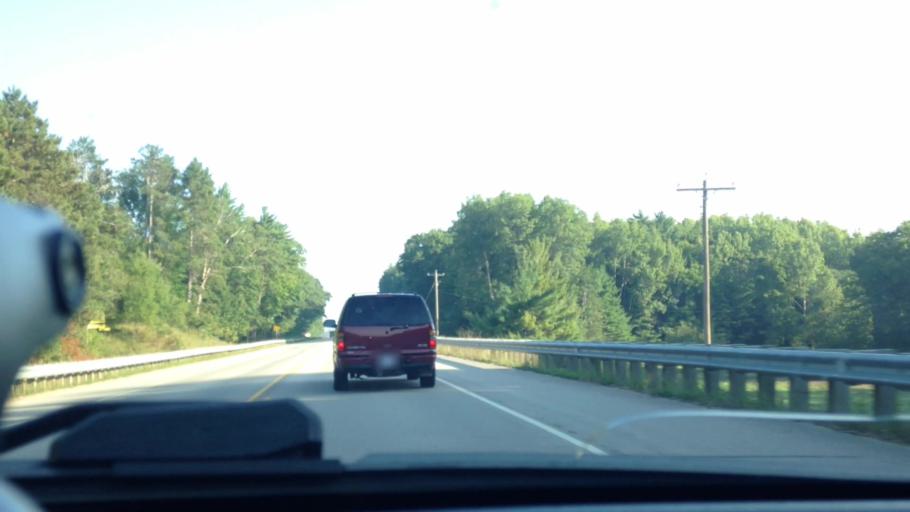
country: US
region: Wisconsin
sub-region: Marinette County
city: Peshtigo
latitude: 45.1684
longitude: -87.9963
